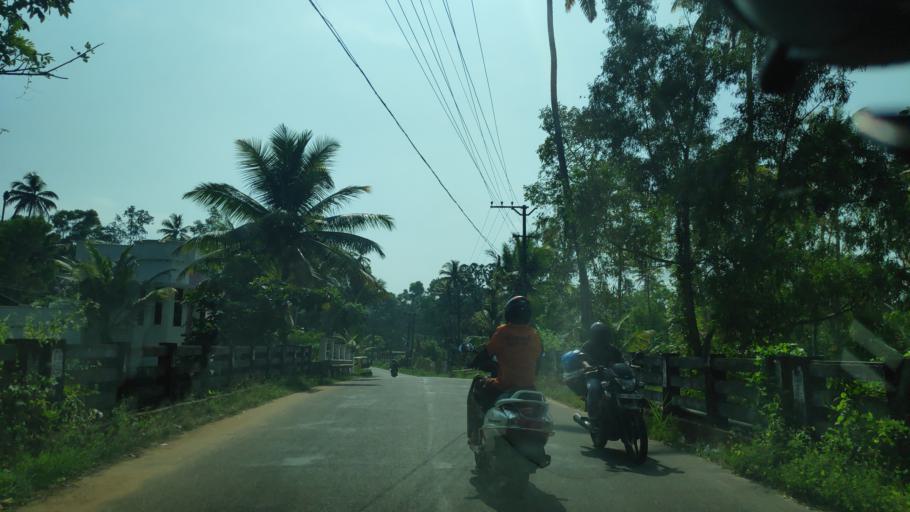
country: IN
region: Kerala
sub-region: Alappuzha
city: Vayalar
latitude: 9.6488
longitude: 76.2999
